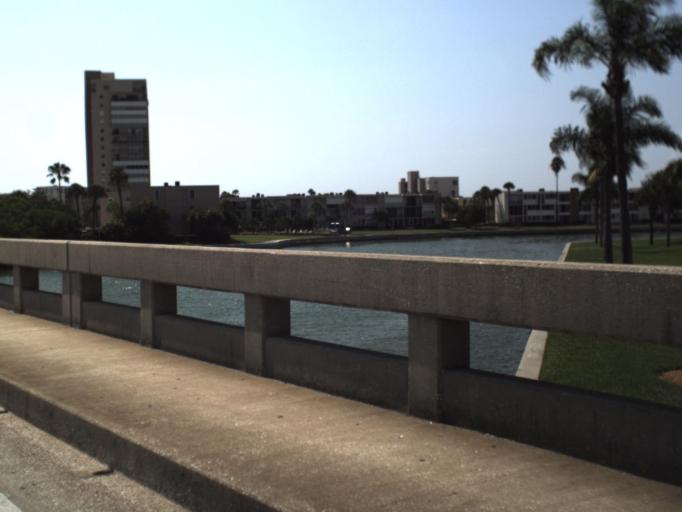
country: US
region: Florida
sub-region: Pinellas County
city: South Pasadena
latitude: 27.7515
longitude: -82.7406
